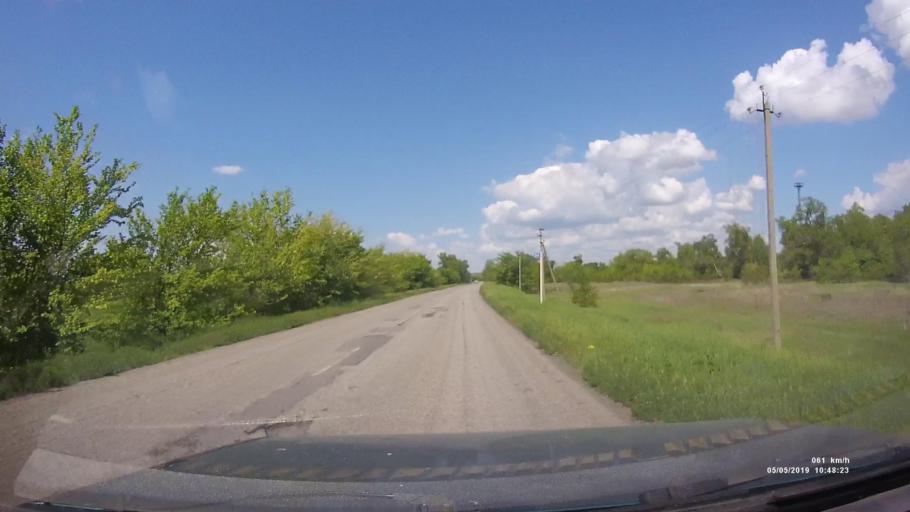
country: RU
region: Rostov
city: Ust'-Donetskiy
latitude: 47.6424
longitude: 40.8206
